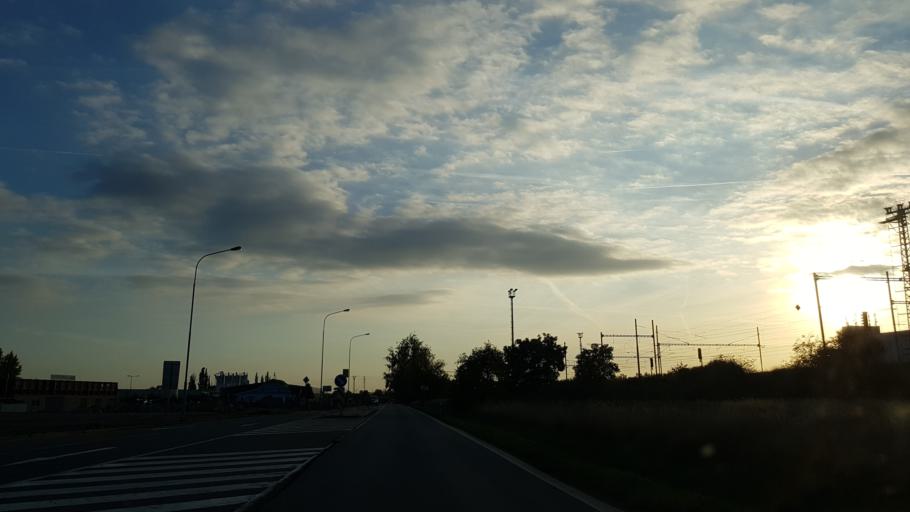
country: CZ
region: Zlin
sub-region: Okres Uherske Hradiste
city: Stare Mesto
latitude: 49.0722
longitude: 17.4196
